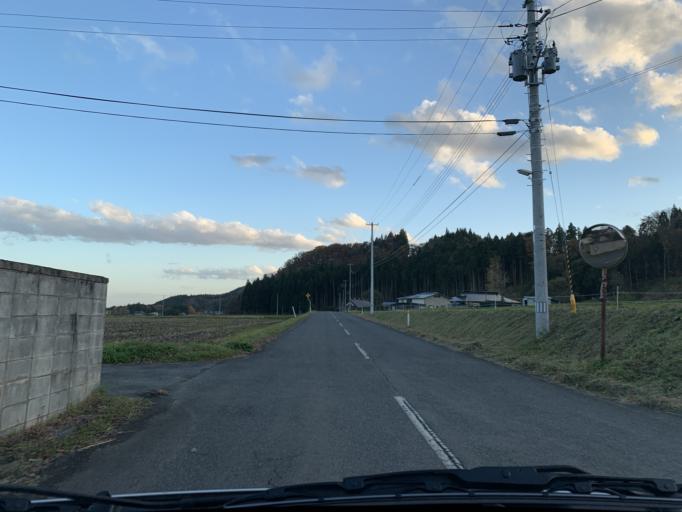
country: JP
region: Iwate
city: Mizusawa
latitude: 39.0421
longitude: 141.0507
